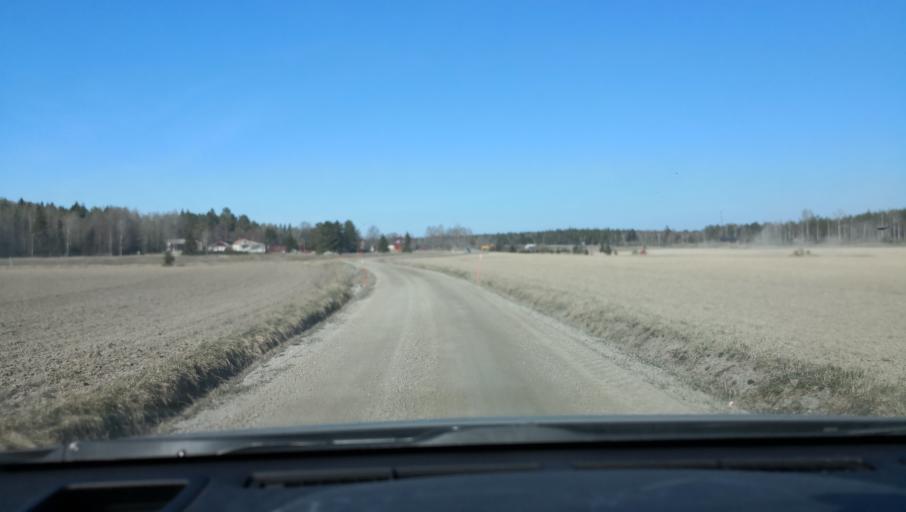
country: SE
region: Vaestmanland
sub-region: Sala Kommun
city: Sala
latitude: 59.9017
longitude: 16.5300
